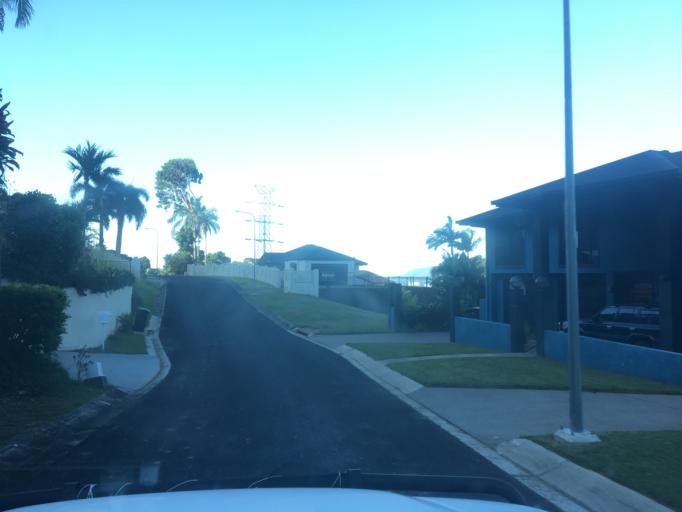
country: AU
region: Queensland
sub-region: Cairns
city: Woree
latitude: -16.9353
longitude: 145.7222
